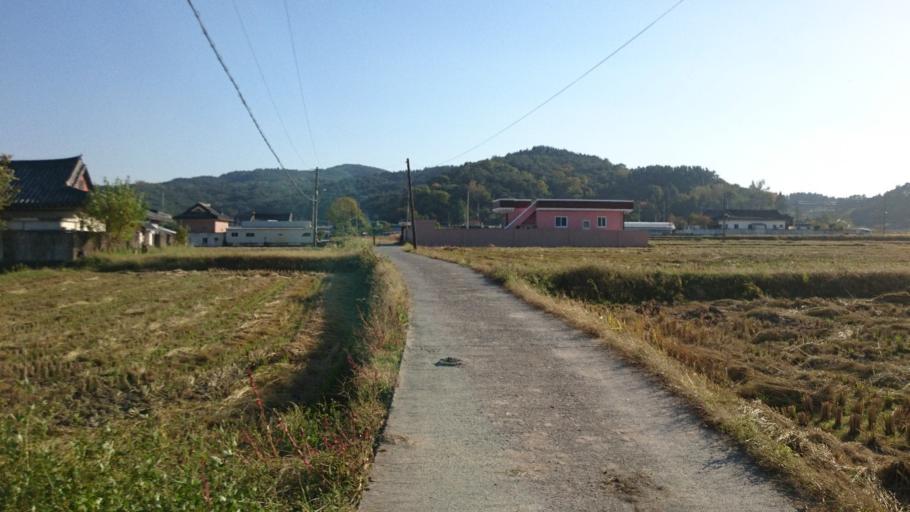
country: KR
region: Gyeongsangbuk-do
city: Kyonju
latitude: 35.8290
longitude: 129.2254
